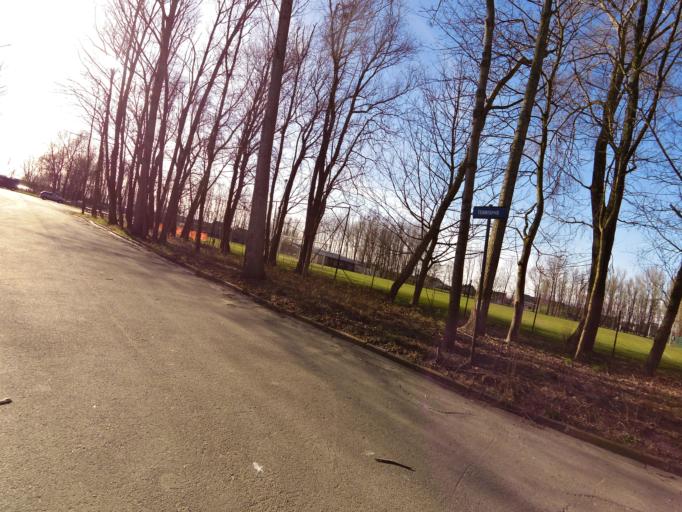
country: BE
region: Flanders
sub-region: Provincie West-Vlaanderen
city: Ostend
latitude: 51.2024
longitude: 2.9214
